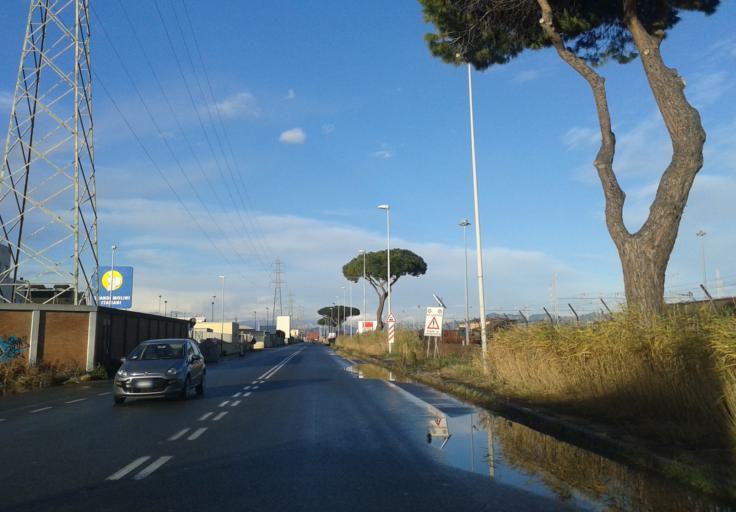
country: IT
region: Tuscany
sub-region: Provincia di Livorno
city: Livorno
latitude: 43.5782
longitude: 10.3219
